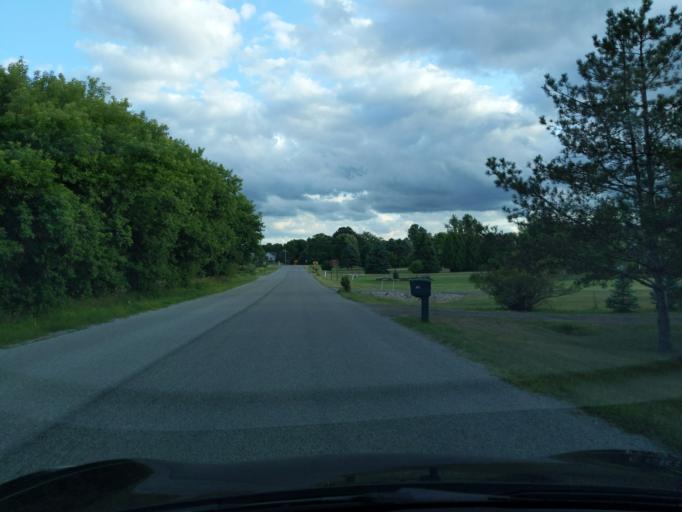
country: US
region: Michigan
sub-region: Ingham County
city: Holt
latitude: 42.5996
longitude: -84.5822
